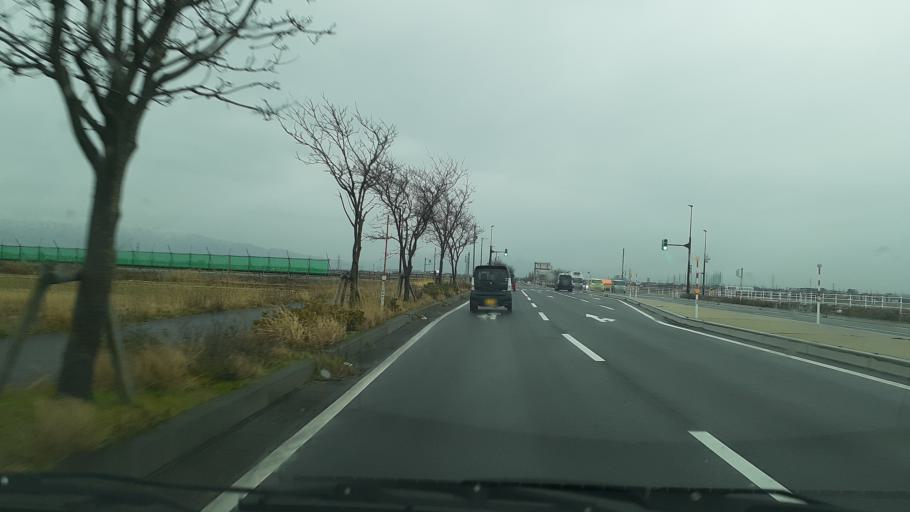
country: JP
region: Niigata
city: Kameda-honcho
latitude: 37.8671
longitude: 139.1388
